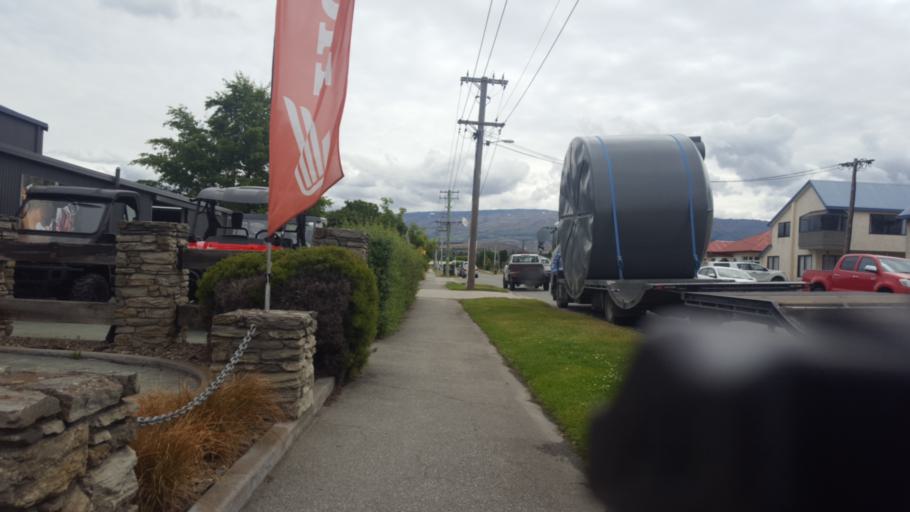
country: NZ
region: Otago
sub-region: Queenstown-Lakes District
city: Wanaka
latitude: -45.2500
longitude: 169.3864
